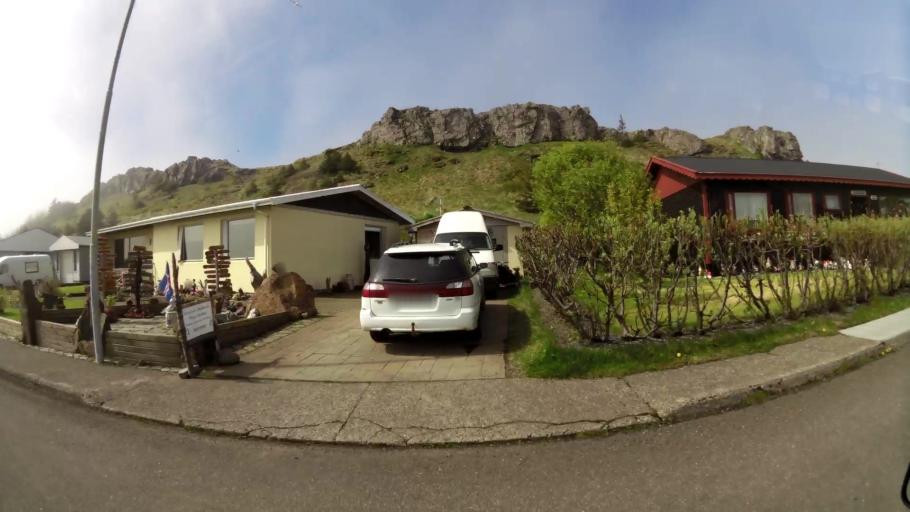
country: IS
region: East
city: Reydarfjoerdur
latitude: 64.6544
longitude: -14.2815
